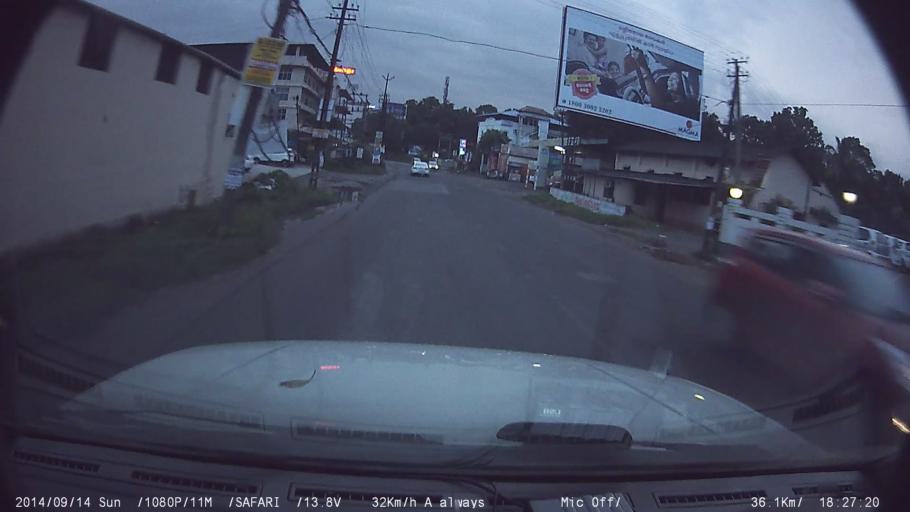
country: IN
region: Kerala
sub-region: Kottayam
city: Kottayam
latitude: 9.6015
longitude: 76.5319
